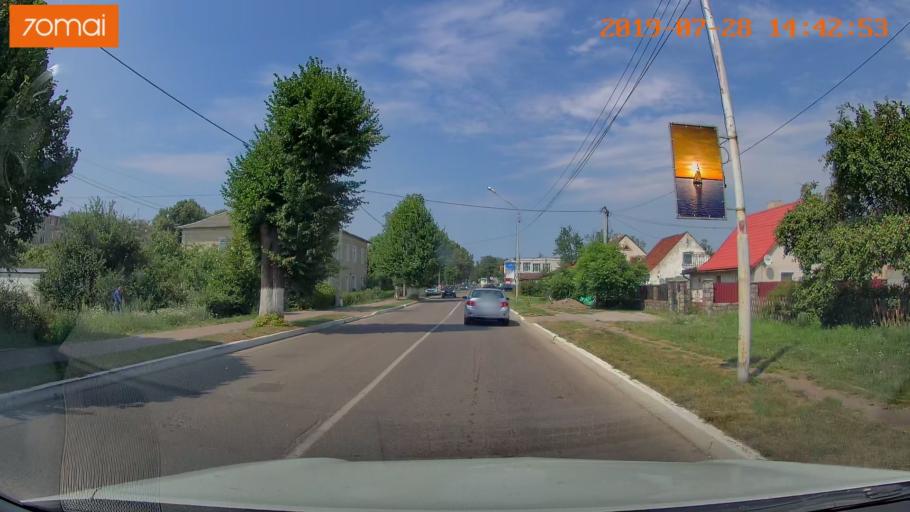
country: RU
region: Kaliningrad
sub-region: Gorod Kaliningrad
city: Yantarnyy
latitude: 54.8624
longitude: 19.9404
